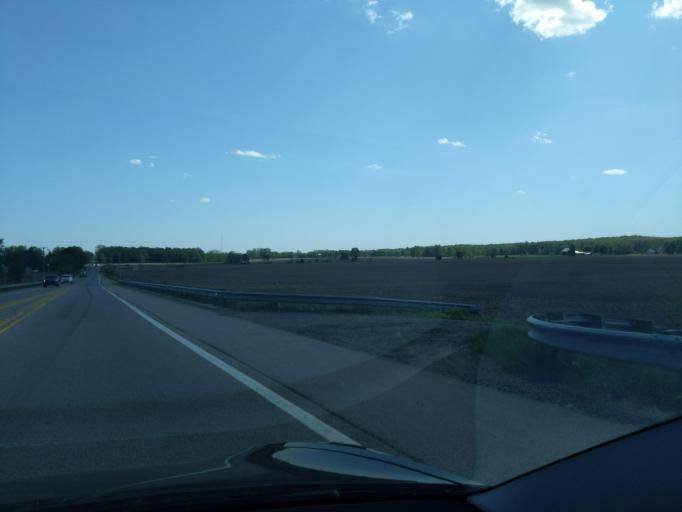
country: US
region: Michigan
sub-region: Kent County
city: Lowell
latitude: 42.8766
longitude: -85.3710
